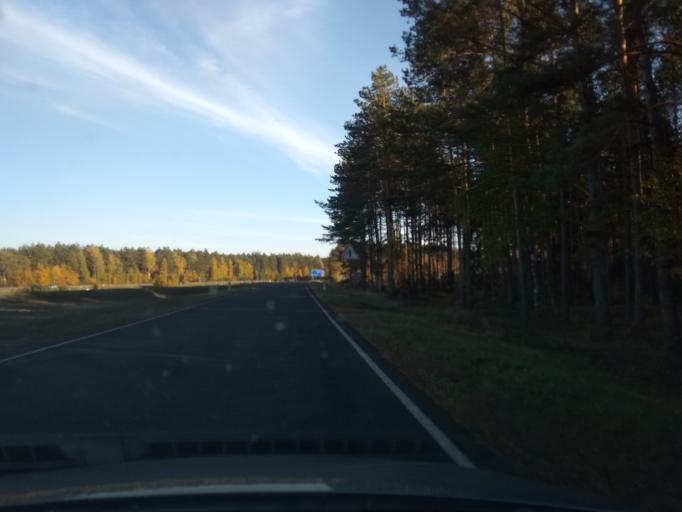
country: BY
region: Brest
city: Nyakhachava
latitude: 52.5734
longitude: 25.1105
